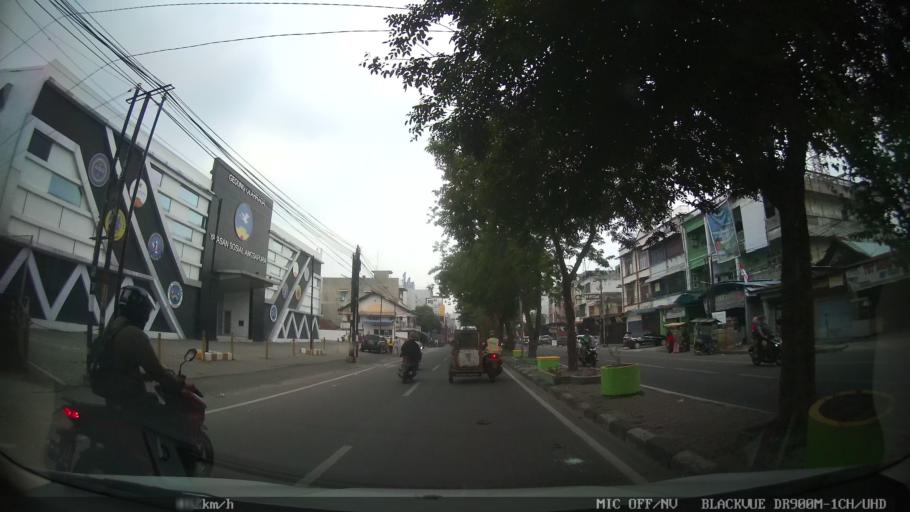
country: ID
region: North Sumatra
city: Medan
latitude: 3.5753
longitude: 98.7034
